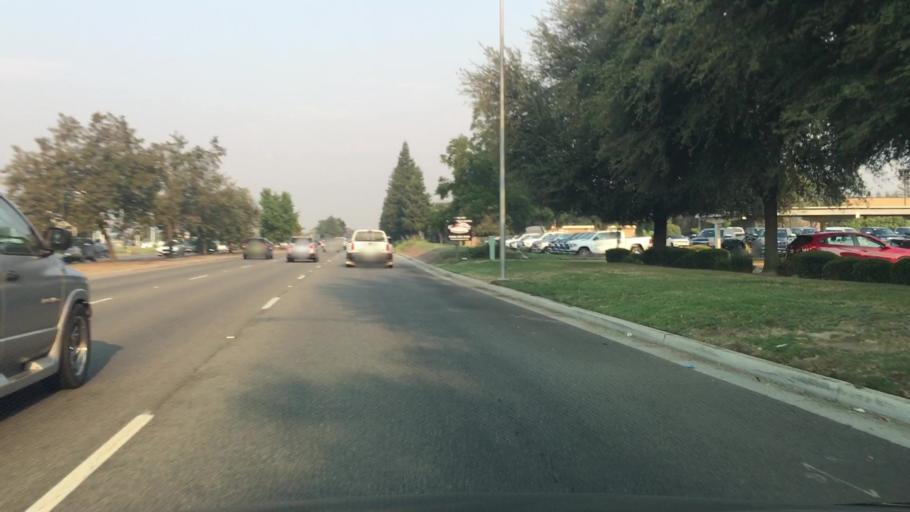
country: US
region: California
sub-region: Fresno County
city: Clovis
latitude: 36.8377
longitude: -119.7152
